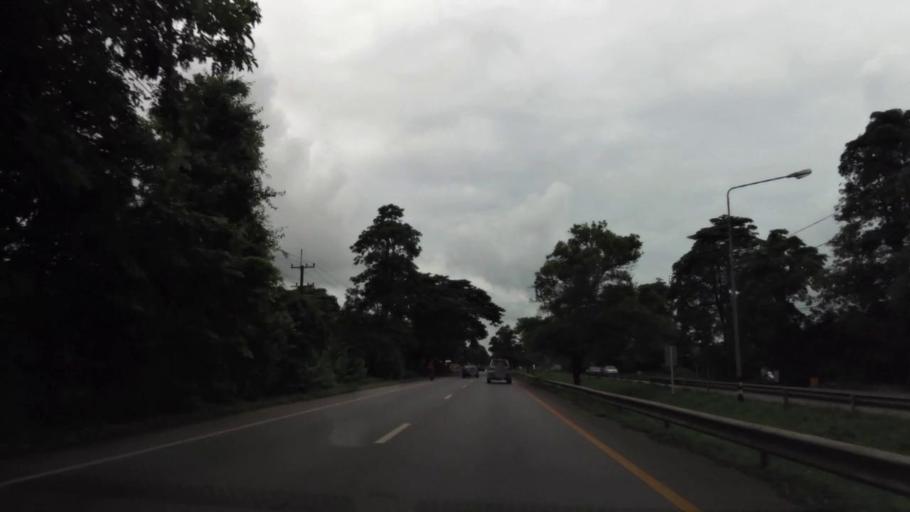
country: TH
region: Chanthaburi
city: Tha Mai
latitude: 12.6493
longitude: 102.0315
